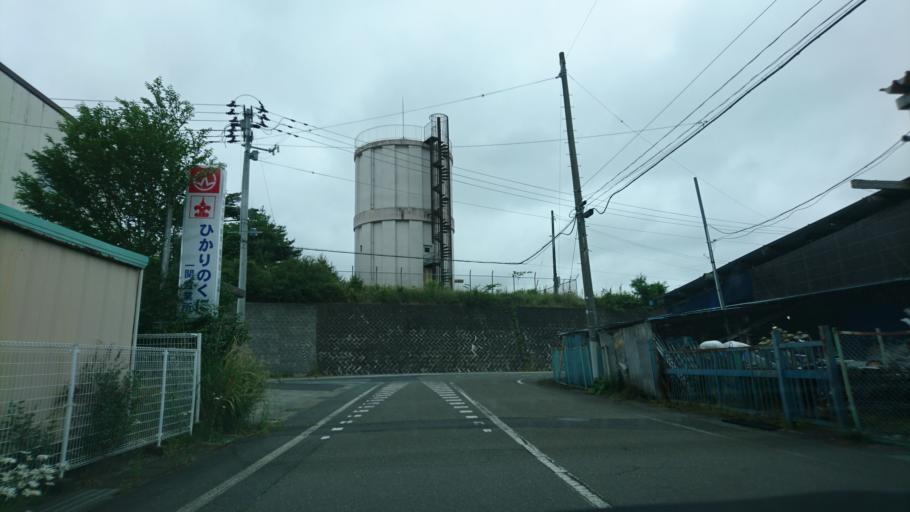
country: JP
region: Iwate
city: Ichinoseki
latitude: 38.9035
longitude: 141.1616
